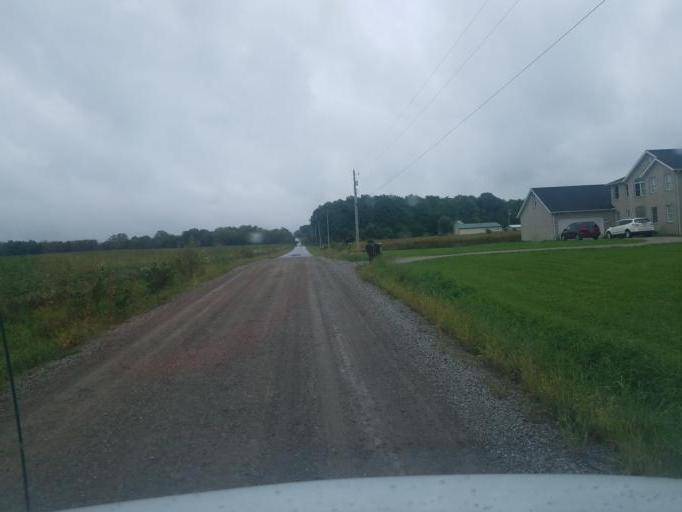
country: US
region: Ohio
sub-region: Wayne County
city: West Salem
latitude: 40.9300
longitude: -82.1069
